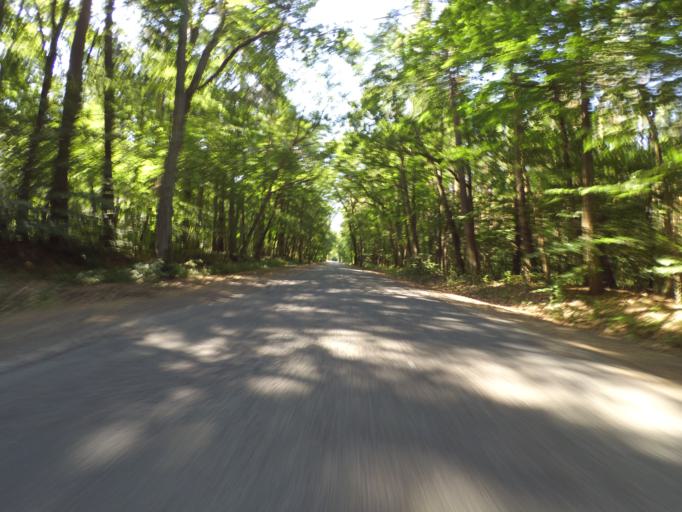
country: DE
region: Brandenburg
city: Triglitz
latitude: 53.2279
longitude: 12.1126
